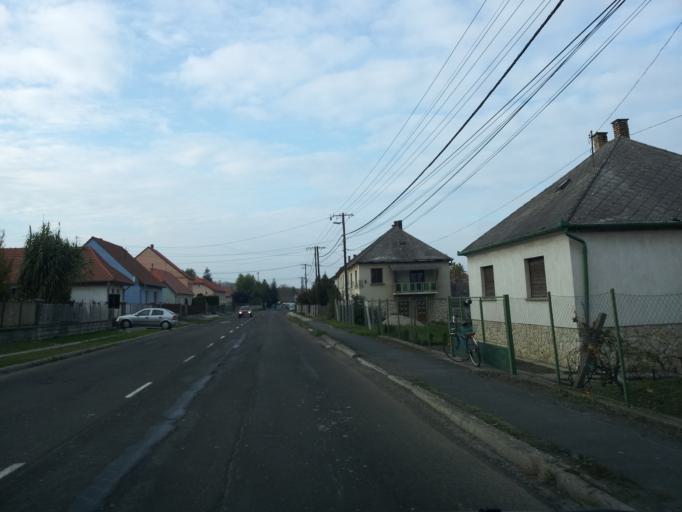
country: HU
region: Gyor-Moson-Sopron
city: Pannonhalma
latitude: 47.5193
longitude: 17.7515
